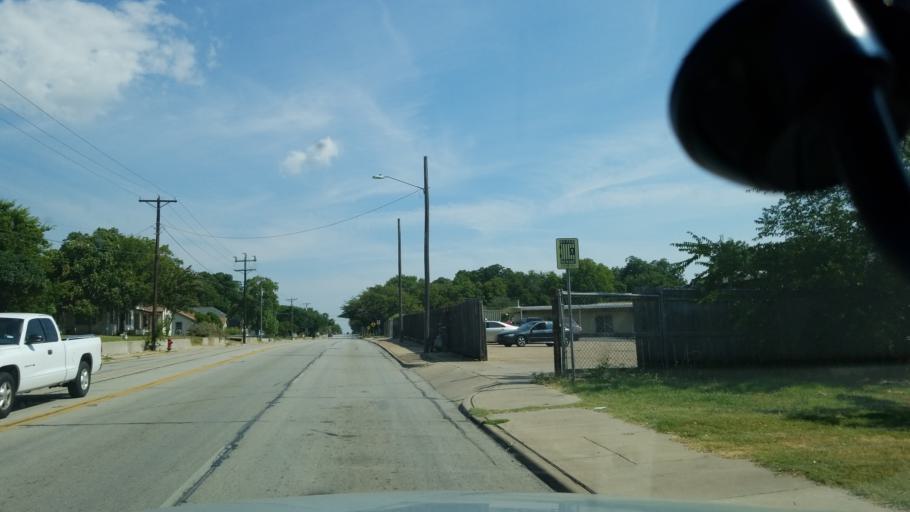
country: US
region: Texas
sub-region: Dallas County
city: Grand Prairie
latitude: 32.7501
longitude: -96.9603
